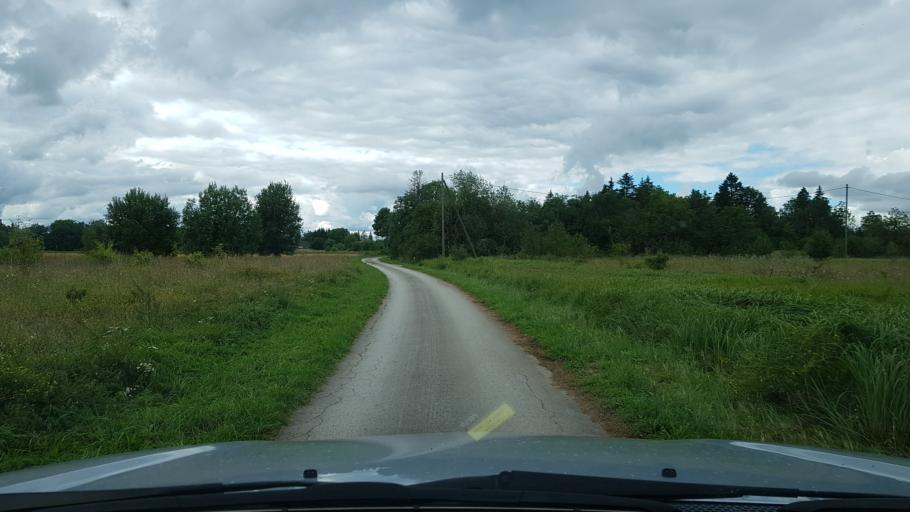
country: EE
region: Harju
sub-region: Rae vald
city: Vaida
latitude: 59.2753
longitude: 25.0125
